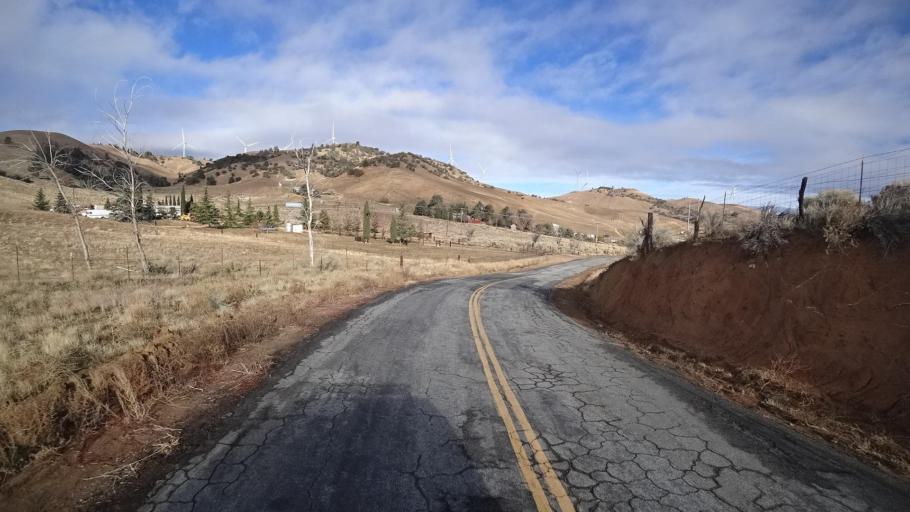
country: US
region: California
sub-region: Kern County
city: Tehachapi
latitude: 35.0724
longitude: -118.3426
